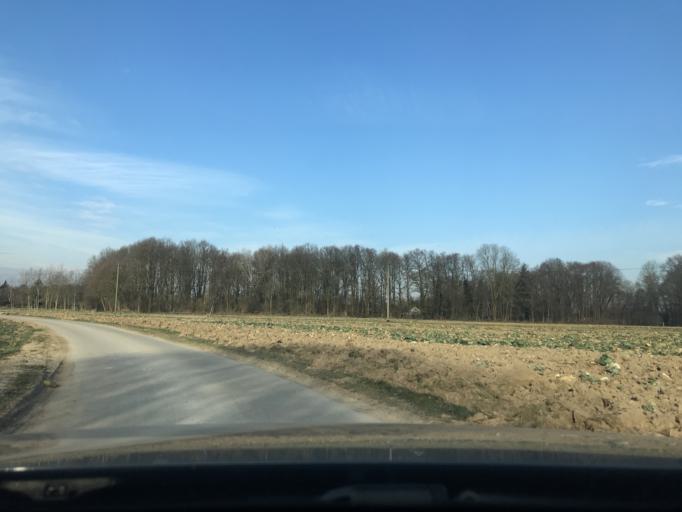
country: DE
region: North Rhine-Westphalia
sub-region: Regierungsbezirk Dusseldorf
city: Grefrath
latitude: 51.3377
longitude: 6.3781
